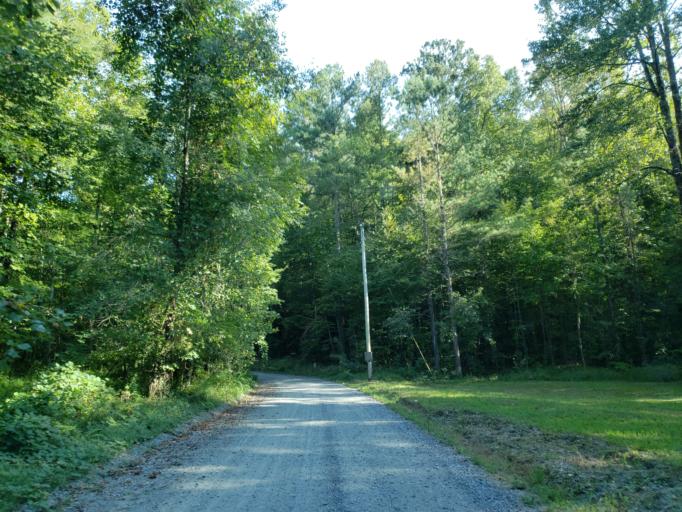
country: US
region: Georgia
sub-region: Fannin County
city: Blue Ridge
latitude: 34.6843
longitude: -84.2668
